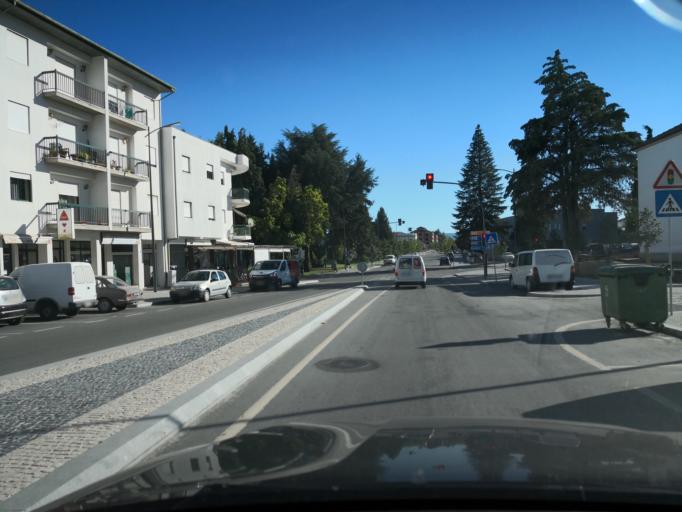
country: PT
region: Vila Real
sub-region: Valpacos
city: Valpacos
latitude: 41.6105
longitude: -7.3131
